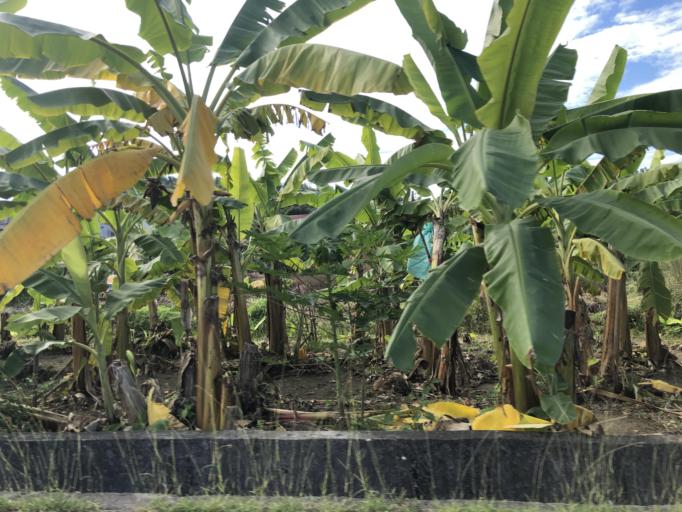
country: TW
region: Taiwan
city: Yujing
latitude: 23.0455
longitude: 120.4222
